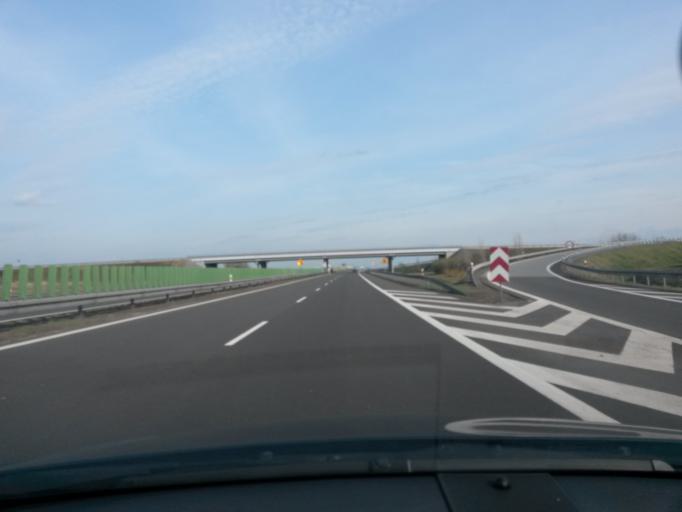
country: PL
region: Greater Poland Voivodeship
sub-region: Powiat wrzesinski
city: Wrzesnia
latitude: 52.3157
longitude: 17.5310
